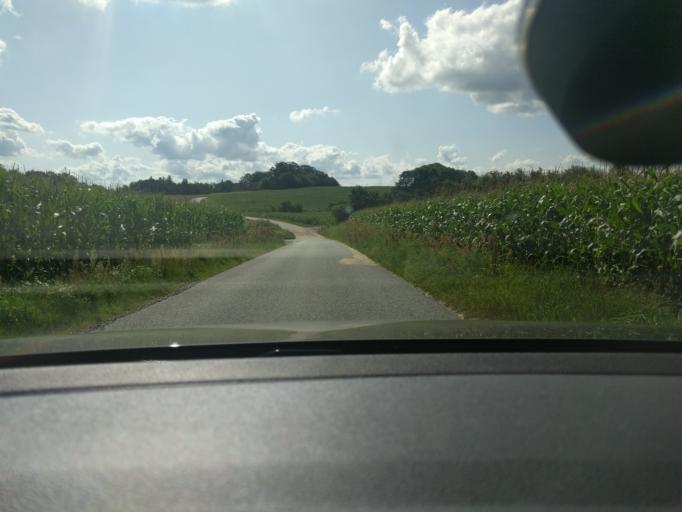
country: DK
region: Central Jutland
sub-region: Viborg Kommune
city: Viborg
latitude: 56.5269
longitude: 9.3481
